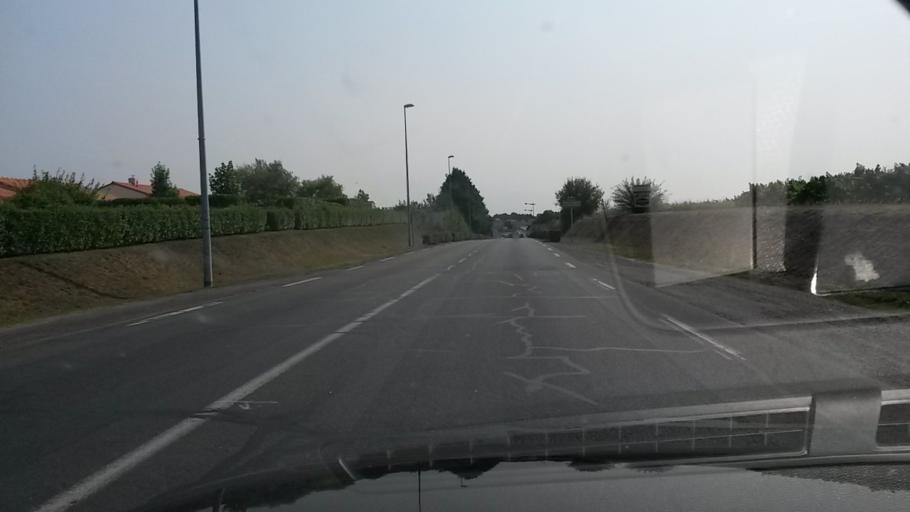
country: FR
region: Pays de la Loire
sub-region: Departement de la Loire-Atlantique
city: Mouzillon
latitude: 47.1444
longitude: -1.2818
